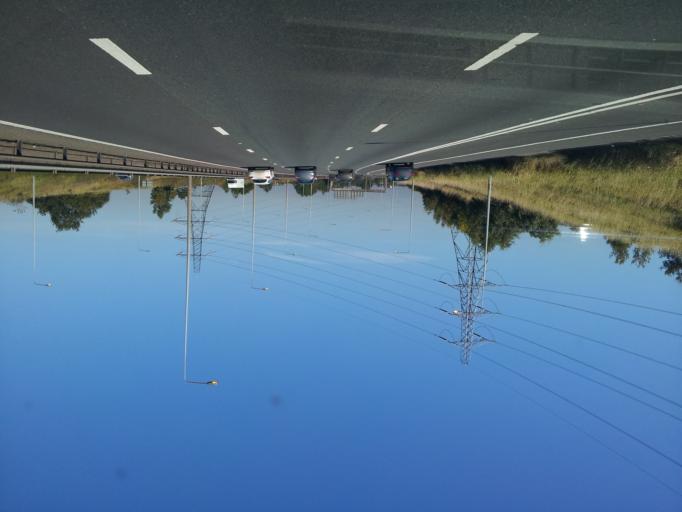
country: GB
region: England
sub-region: Borough of Rochdale
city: Middleton
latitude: 53.5392
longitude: -2.2129
